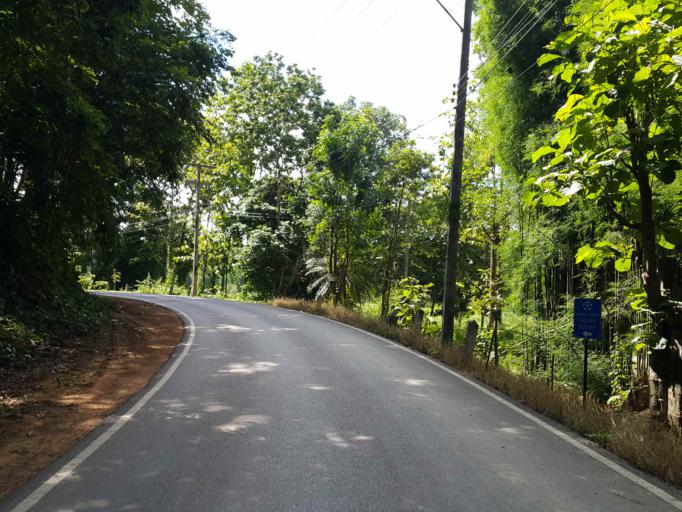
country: TH
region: Chiang Mai
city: Mae Taeng
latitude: 18.9667
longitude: 98.9104
